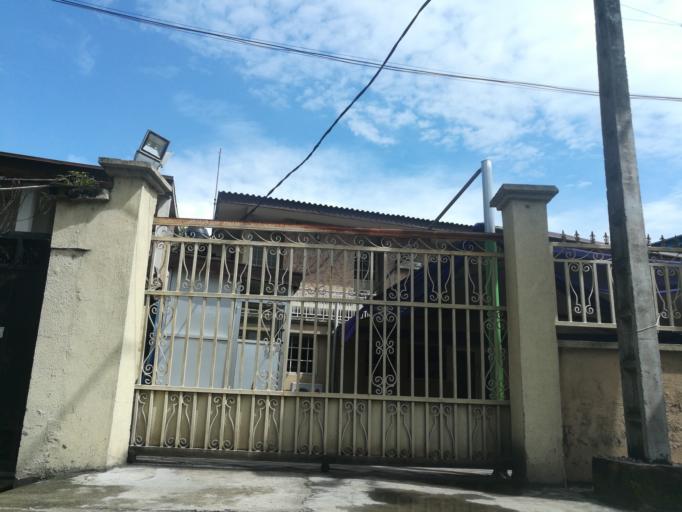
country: NG
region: Lagos
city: Somolu
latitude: 6.5501
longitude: 3.3750
